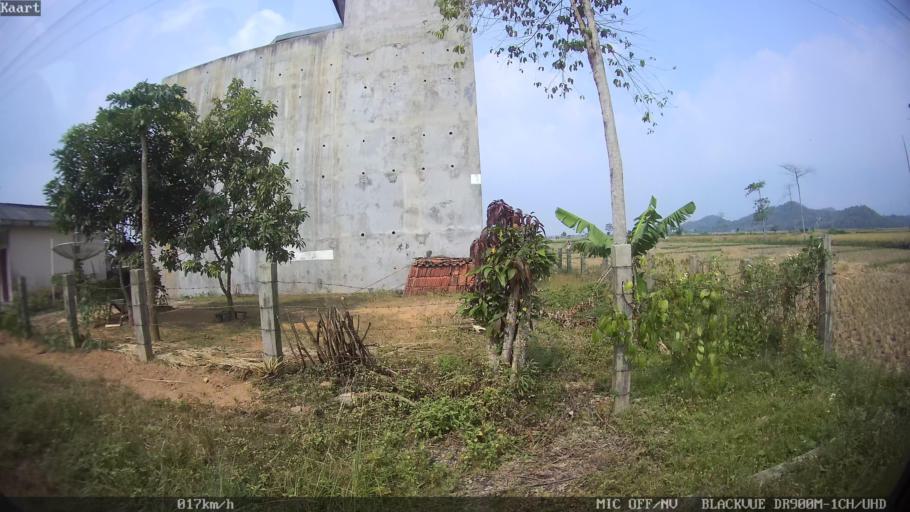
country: ID
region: Lampung
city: Pringsewu
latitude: -5.3721
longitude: 104.9975
